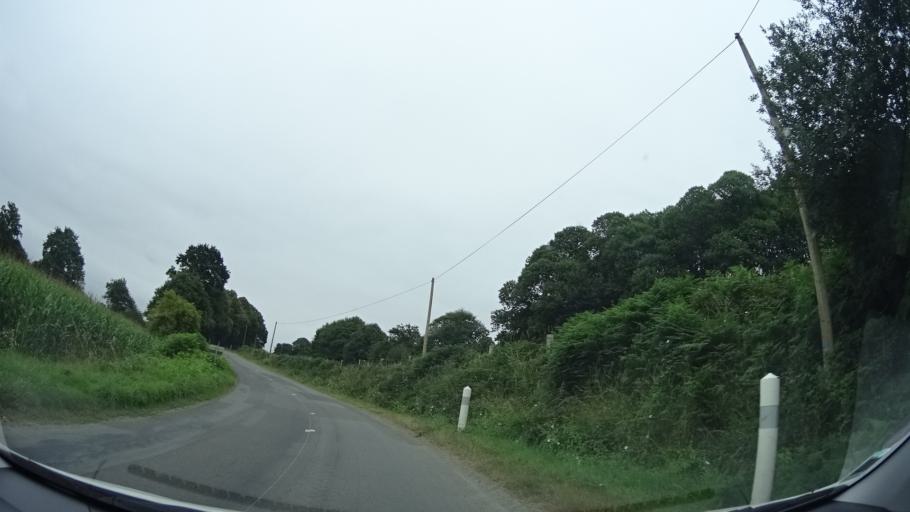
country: FR
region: Brittany
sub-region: Departement d'Ille-et-Vilaine
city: Hede-Bazouges
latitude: 48.3006
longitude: -1.7708
